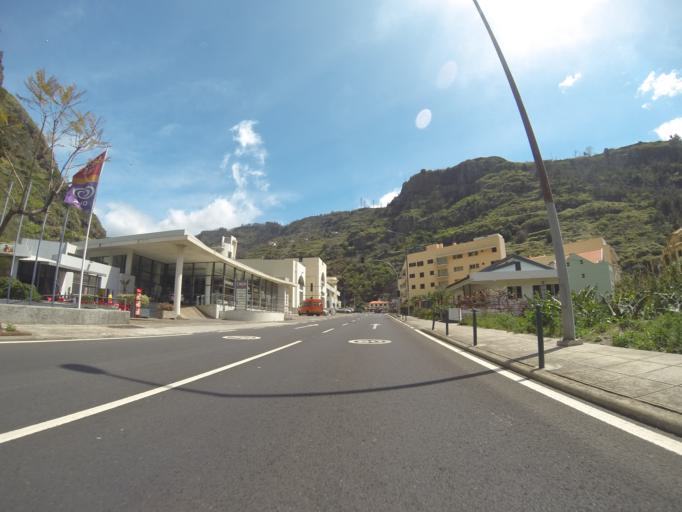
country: PT
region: Madeira
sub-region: Ribeira Brava
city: Campanario
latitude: 32.6799
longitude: -17.0582
